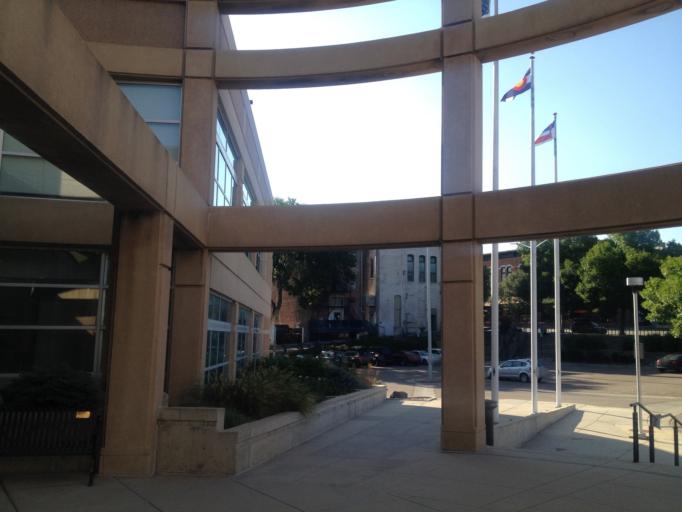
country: US
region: Colorado
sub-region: Boulder County
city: Longmont
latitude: 40.1633
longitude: -105.1012
